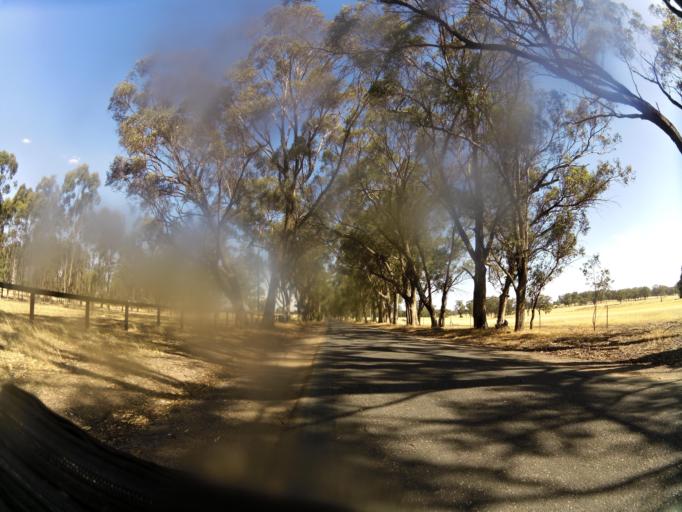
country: AU
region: Victoria
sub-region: Campaspe
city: Kyabram
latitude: -36.8883
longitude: 145.1020
